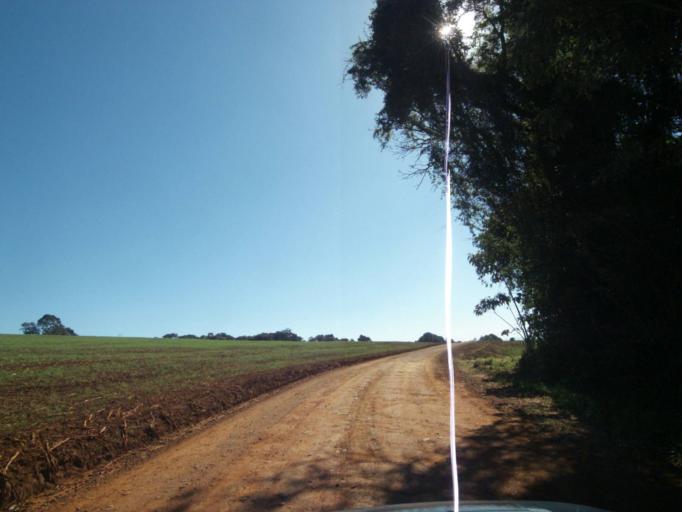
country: BR
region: Parana
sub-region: Tibagi
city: Tibagi
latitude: -24.5765
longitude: -50.6214
